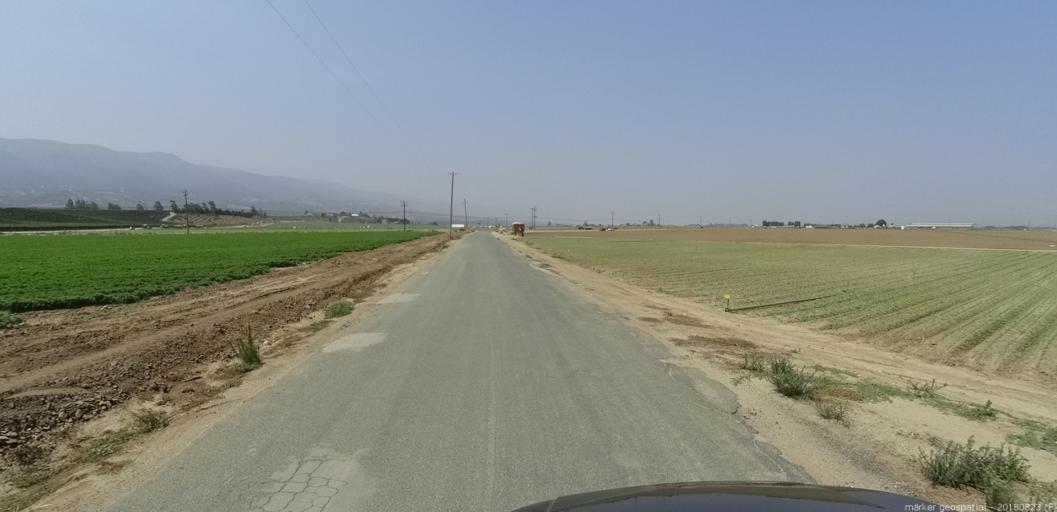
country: US
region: California
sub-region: Monterey County
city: Soledad
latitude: 36.3746
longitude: -121.3250
